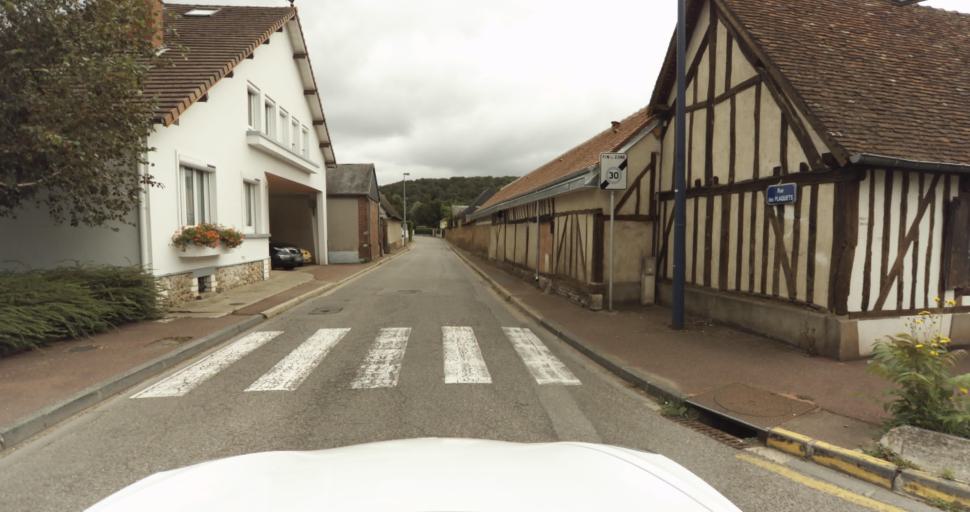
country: FR
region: Haute-Normandie
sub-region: Departement de l'Eure
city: Saint-Sebastien-de-Morsent
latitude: 48.9933
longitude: 1.0410
